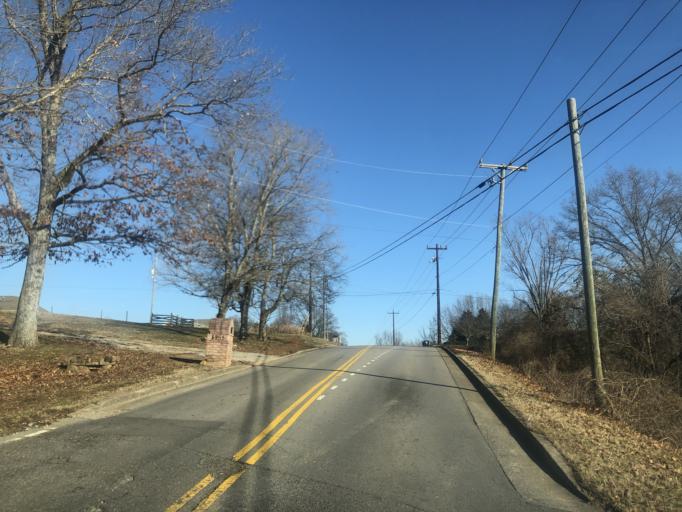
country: US
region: Tennessee
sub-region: Williamson County
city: Nolensville
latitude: 36.0142
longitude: -86.6651
